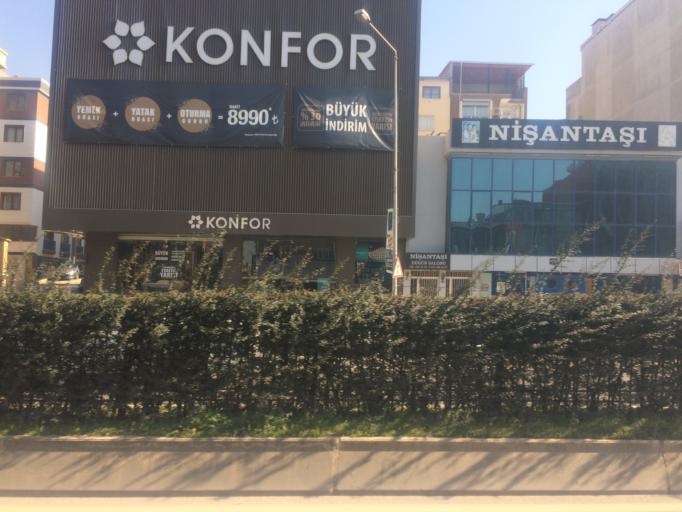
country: TR
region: Izmir
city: Karsiyaka
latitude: 38.4992
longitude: 27.0563
